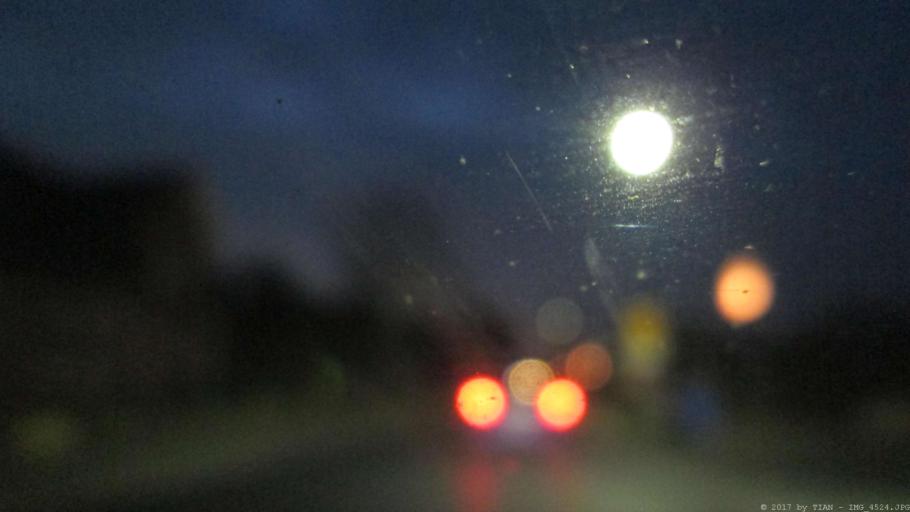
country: DE
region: Lower Saxony
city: Wieren
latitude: 52.8893
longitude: 10.6557
